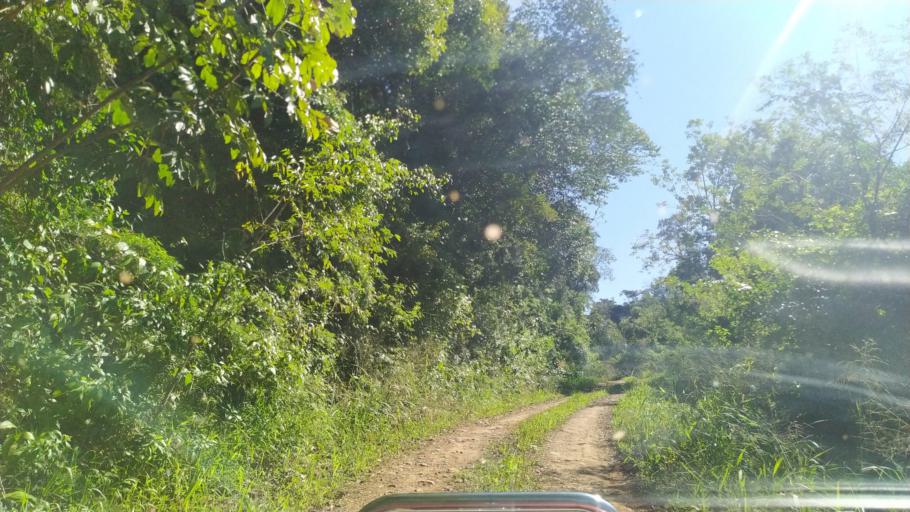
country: AR
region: Misiones
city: El Alcazar
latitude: -26.7604
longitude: -54.5863
